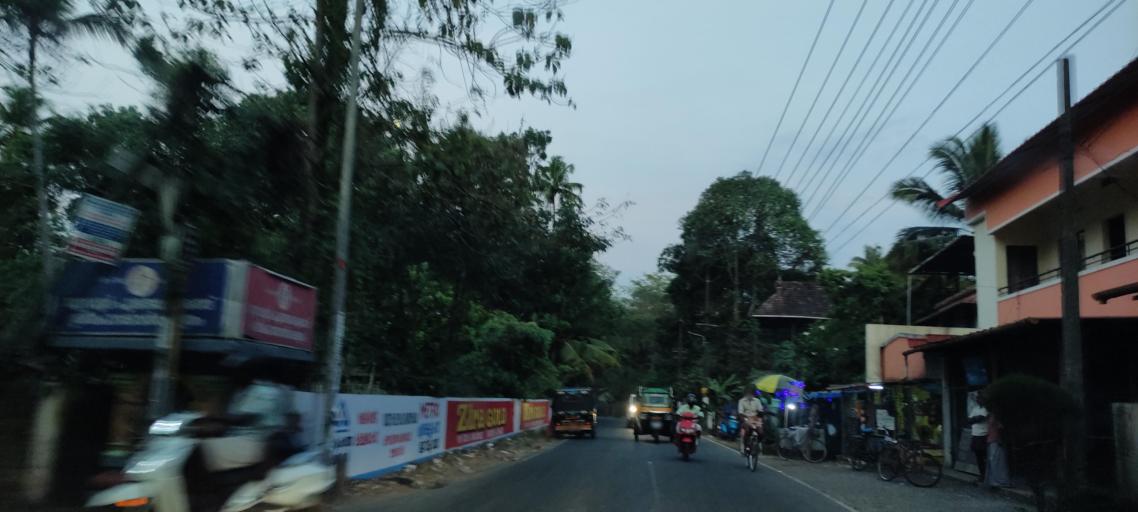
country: IN
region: Kerala
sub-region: Alappuzha
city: Kutiatodu
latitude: 9.7715
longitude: 76.3258
